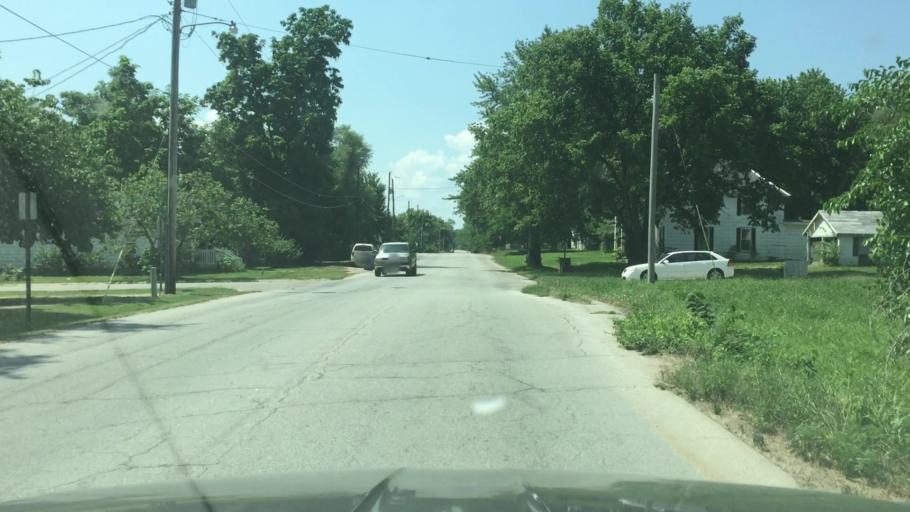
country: US
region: Missouri
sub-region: Miller County
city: Eldon
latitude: 38.3452
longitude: -92.5864
